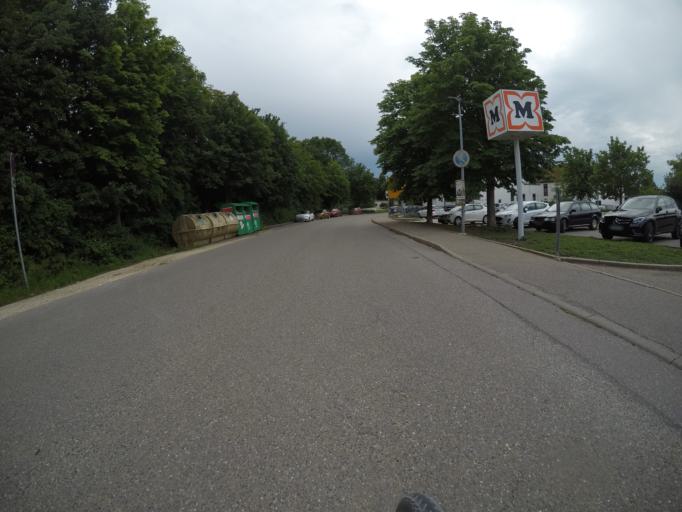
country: DE
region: Baden-Wuerttemberg
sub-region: Tuebingen Region
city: Dornstadt
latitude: 48.4682
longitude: 9.9464
